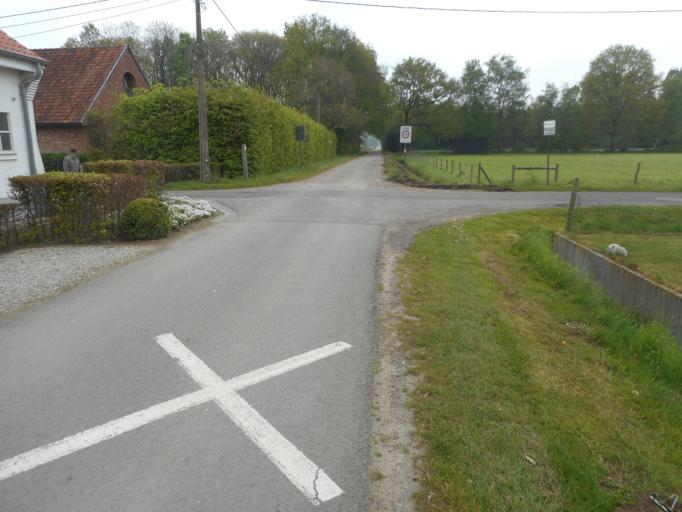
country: BE
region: Flanders
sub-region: Provincie Antwerpen
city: Zoersel
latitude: 51.2371
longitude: 4.7074
